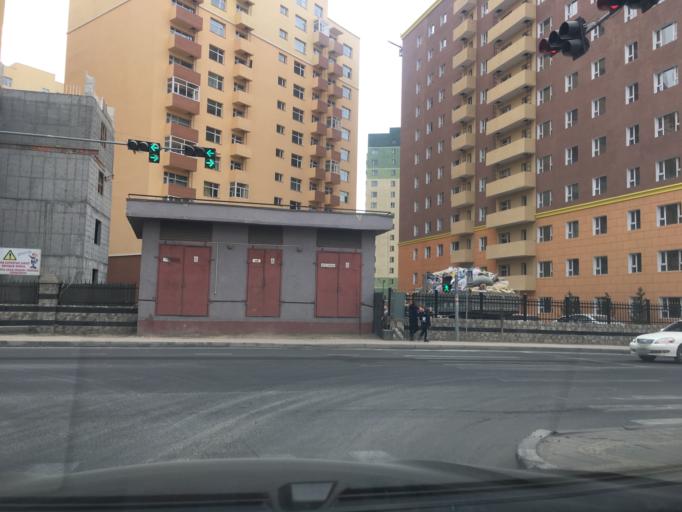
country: MN
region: Ulaanbaatar
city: Ulaanbaatar
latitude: 47.9032
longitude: 106.8829
